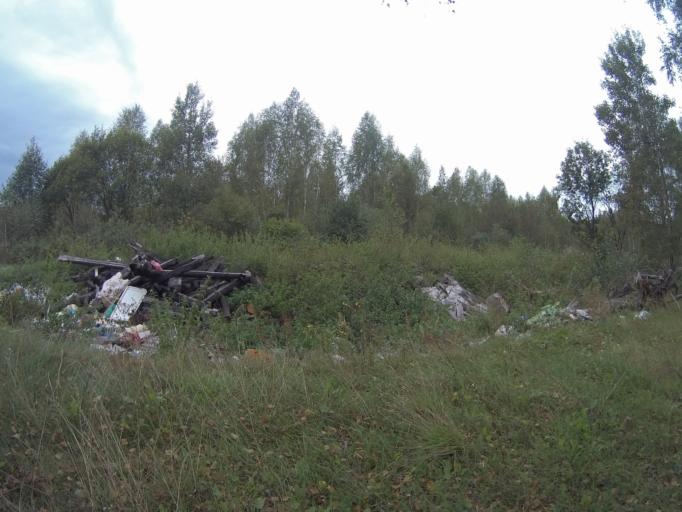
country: RU
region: Vladimir
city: Golovino
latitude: 55.9817
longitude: 40.5091
